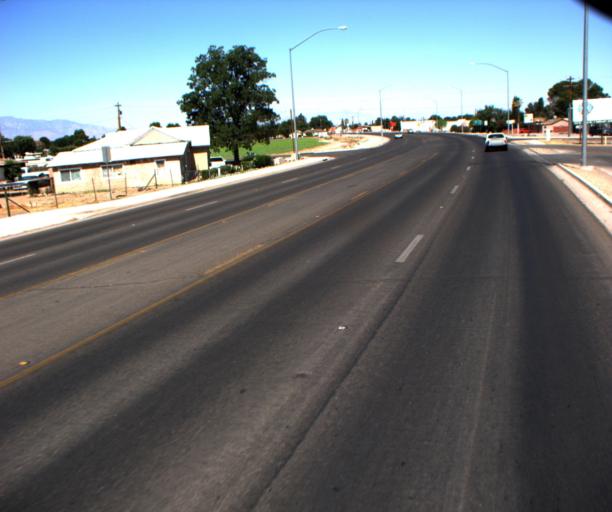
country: US
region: Arizona
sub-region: Graham County
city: Thatcher
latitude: 32.8486
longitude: -109.7490
